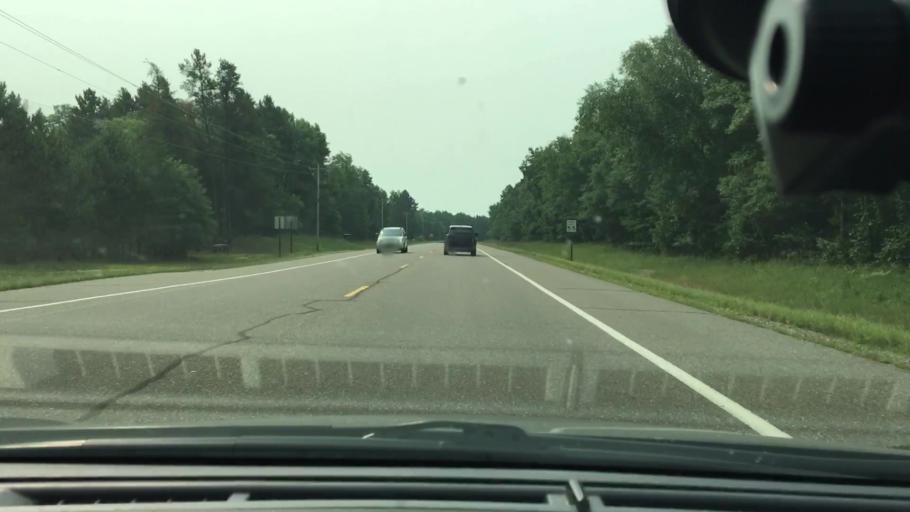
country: US
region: Minnesota
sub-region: Crow Wing County
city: Cross Lake
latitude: 46.5722
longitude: -94.1295
